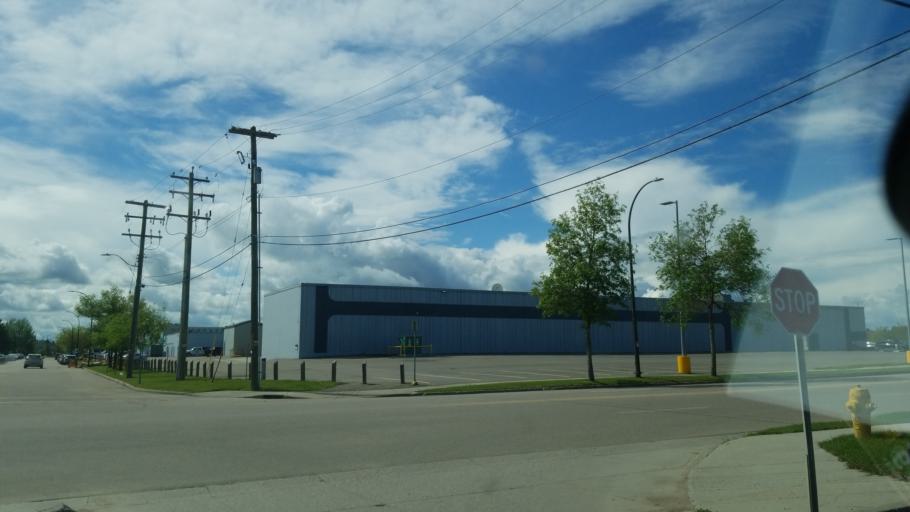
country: CA
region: Saskatchewan
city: Lloydminster
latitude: 53.2761
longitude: -110.0096
